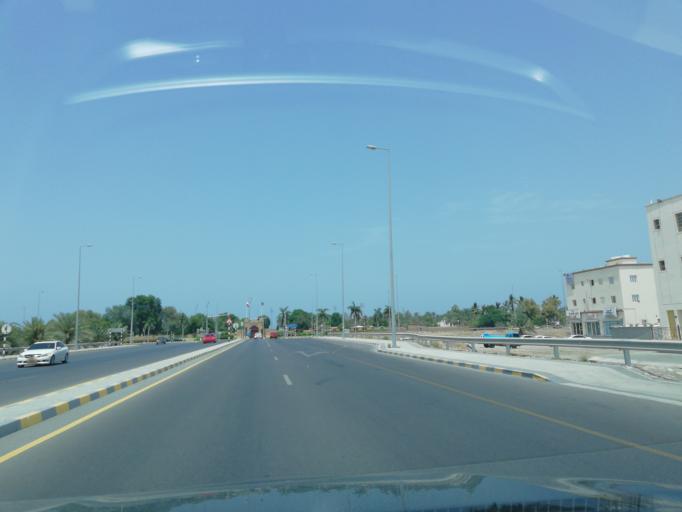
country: OM
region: Muhafazat Masqat
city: As Sib al Jadidah
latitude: 23.6652
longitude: 58.1930
